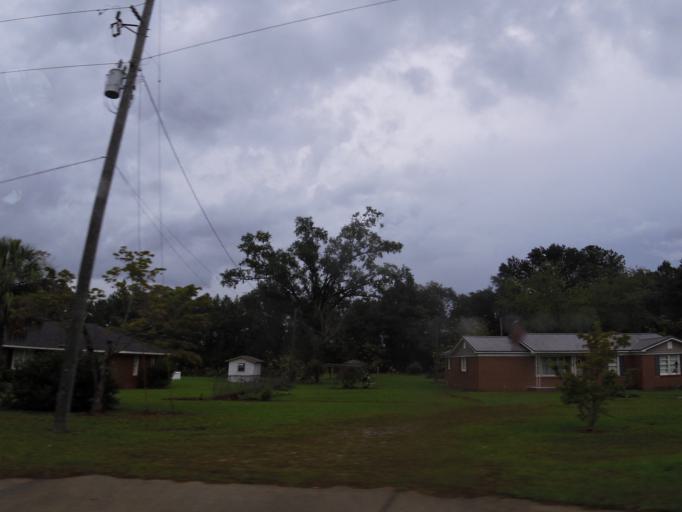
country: US
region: Georgia
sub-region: Wayne County
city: Jesup
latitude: 31.5618
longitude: -81.8344
